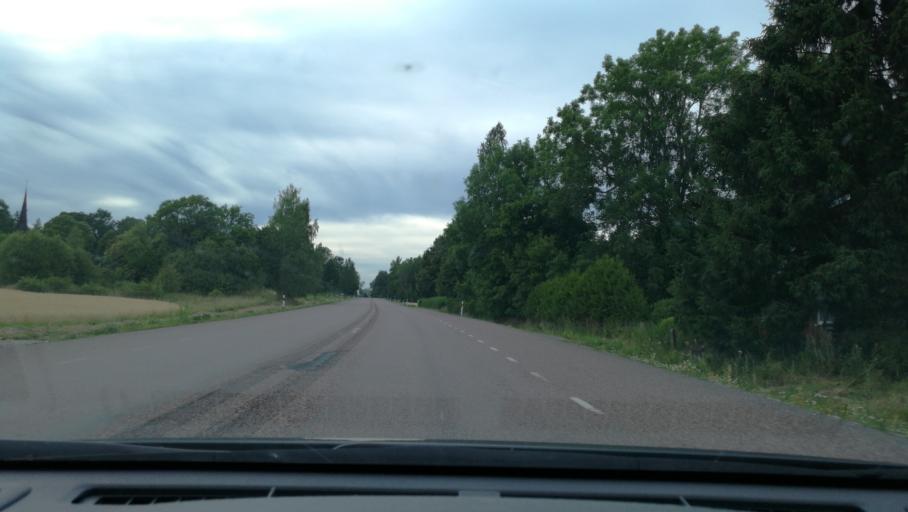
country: SE
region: Vaestmanland
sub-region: Kungsors Kommun
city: Kungsoer
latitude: 59.4478
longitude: 16.0417
